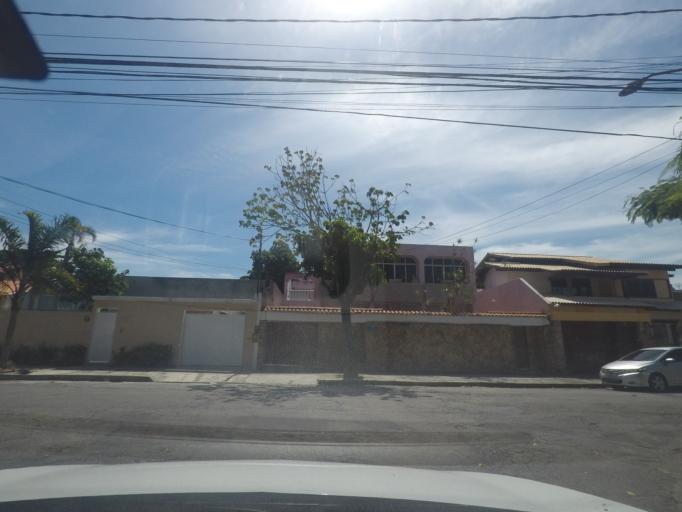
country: BR
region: Rio de Janeiro
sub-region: Niteroi
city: Niteroi
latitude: -22.9180
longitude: -43.0900
